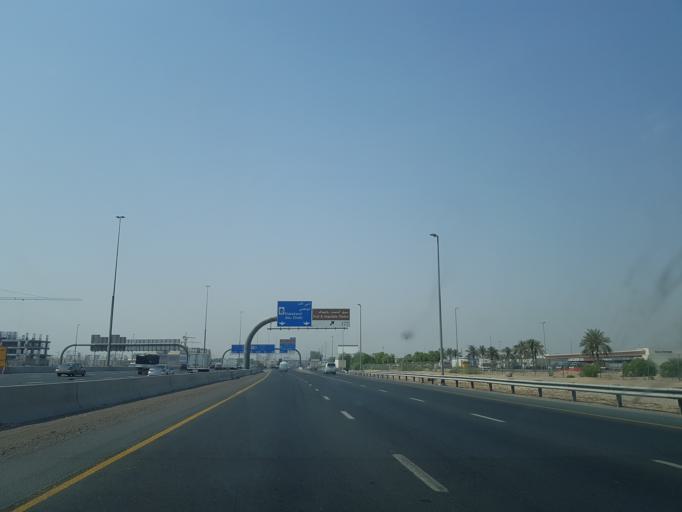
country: AE
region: Ash Shariqah
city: Sharjah
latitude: 25.1721
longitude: 55.3950
